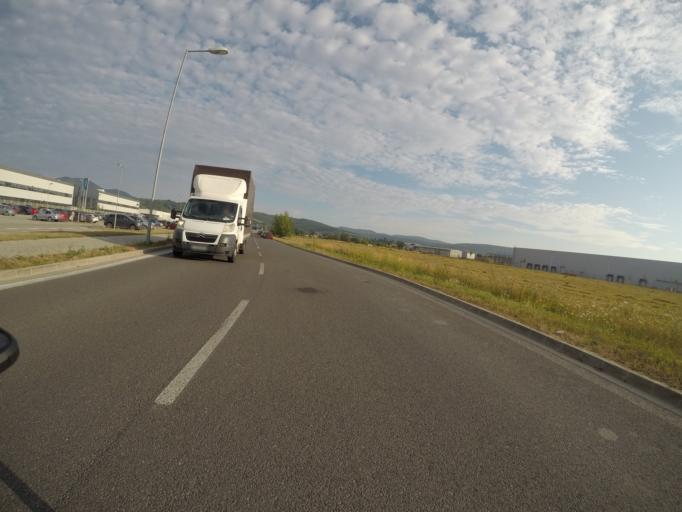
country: SK
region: Trenciansky
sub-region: Okres Trencin
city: Trencin
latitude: 48.8870
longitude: 18.0004
